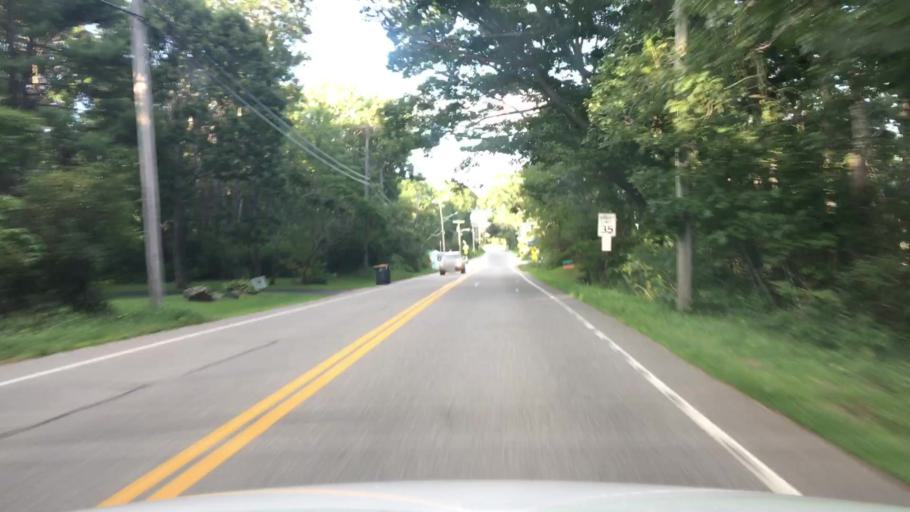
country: US
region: Maine
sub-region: Cumberland County
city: Scarborough
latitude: 43.5656
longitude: -70.2862
